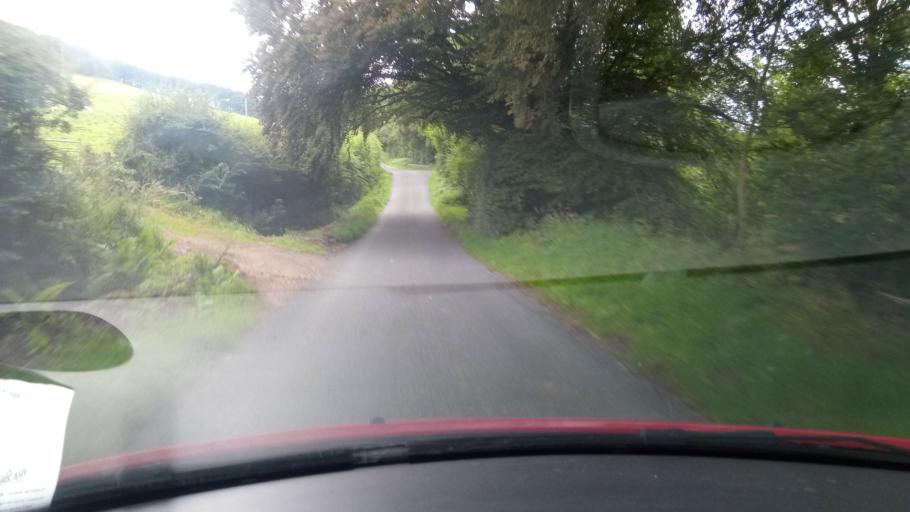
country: GB
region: Scotland
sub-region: The Scottish Borders
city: Jedburgh
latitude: 55.4083
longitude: -2.6450
